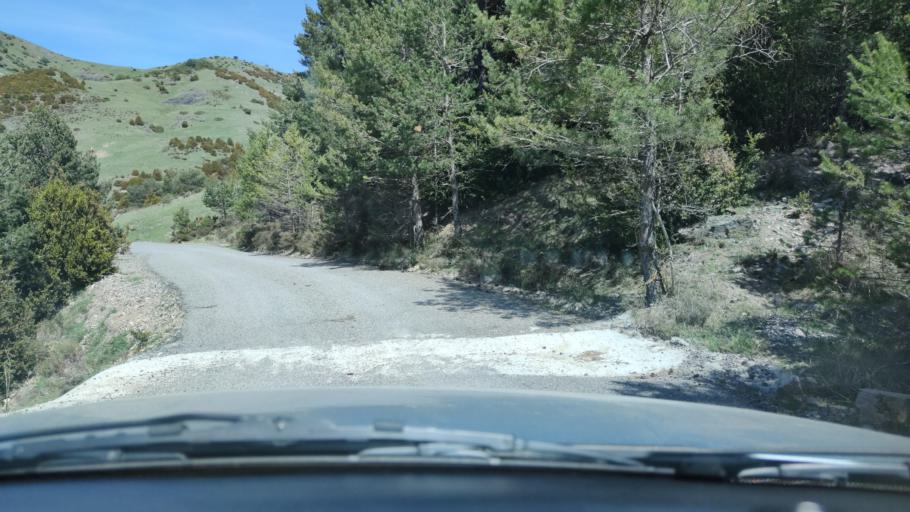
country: ES
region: Catalonia
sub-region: Provincia de Lleida
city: Sort
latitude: 42.3127
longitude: 1.1643
